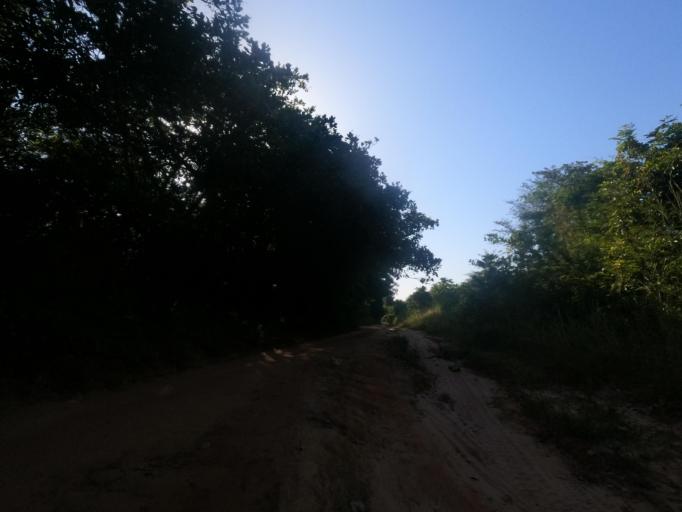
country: GW
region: Cacheu
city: Cacheu
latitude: 12.3942
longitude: -16.2342
